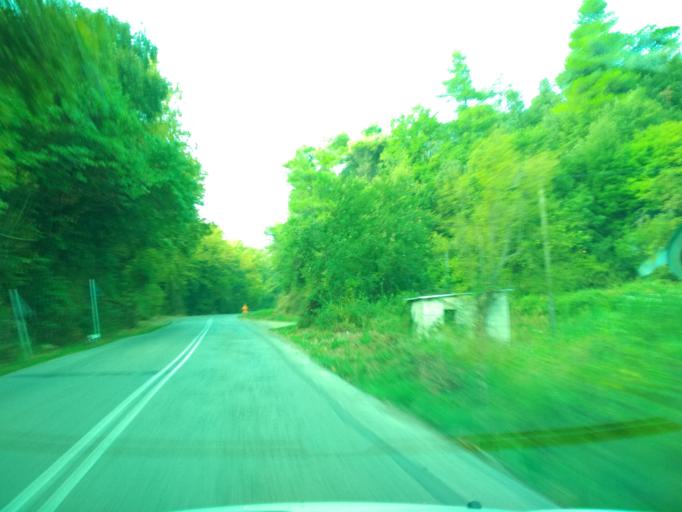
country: GR
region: Central Greece
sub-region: Nomos Evvoias
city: Prokopion
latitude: 38.7538
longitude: 23.4837
